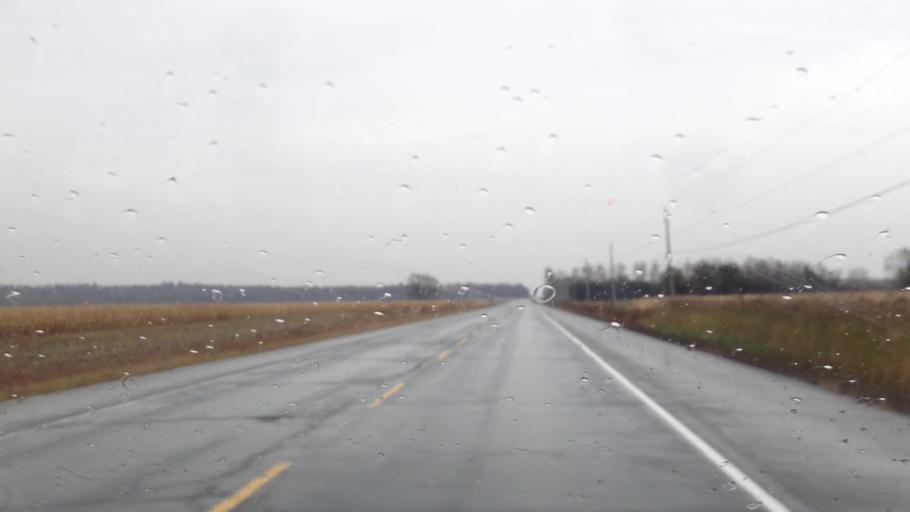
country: CA
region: Ontario
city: Clarence-Rockland
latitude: 45.4450
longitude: -75.4208
